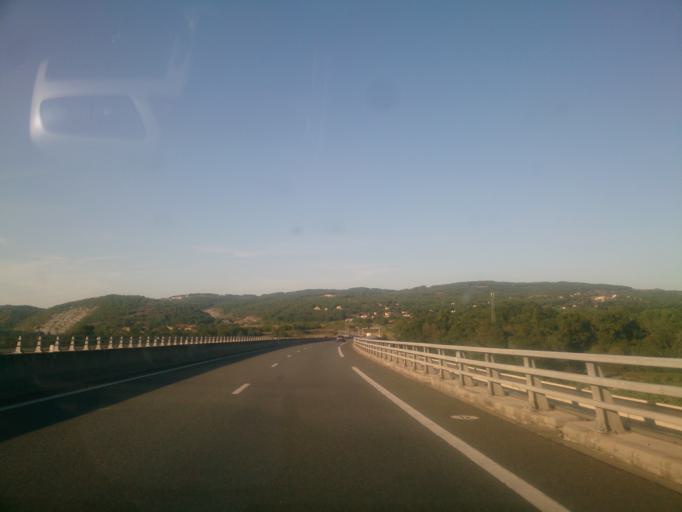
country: FR
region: Midi-Pyrenees
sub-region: Departement du Lot
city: Souillac
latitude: 44.8501
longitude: 1.4933
